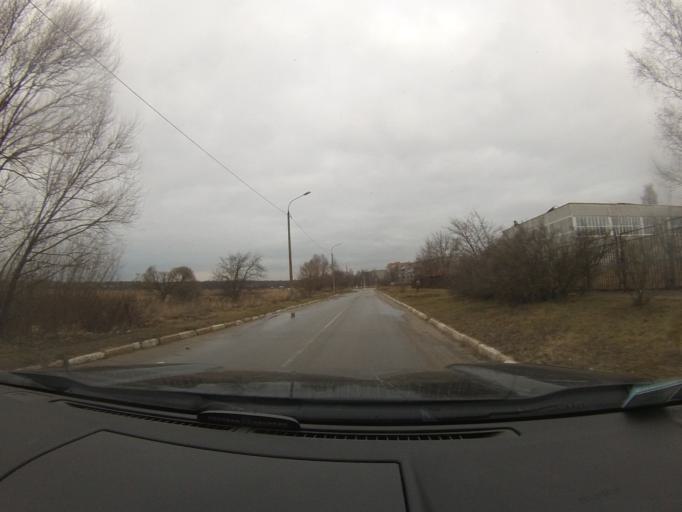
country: RU
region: Moskovskaya
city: Lopatinskiy
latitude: 55.3378
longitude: 38.7098
